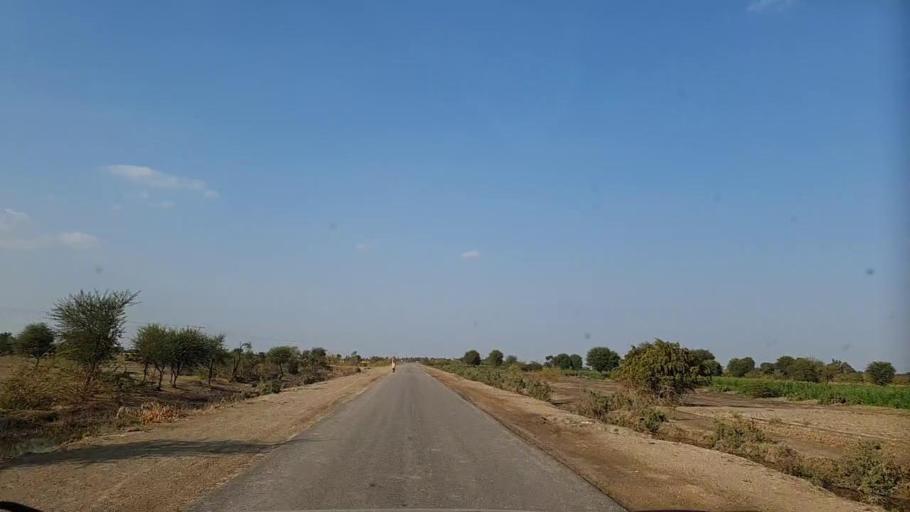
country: PK
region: Sindh
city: Pithoro
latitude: 25.7021
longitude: 69.2223
